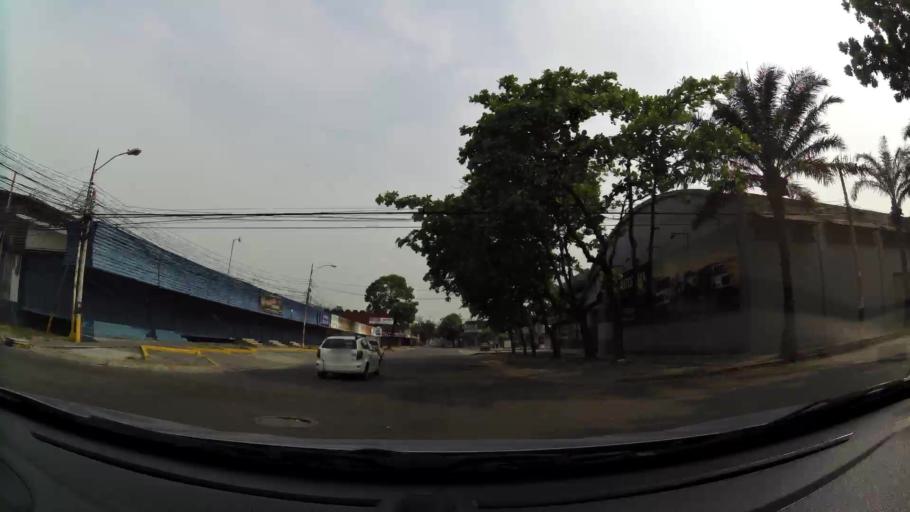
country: HN
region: Cortes
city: San Pedro Sula
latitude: 15.5149
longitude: -88.0237
